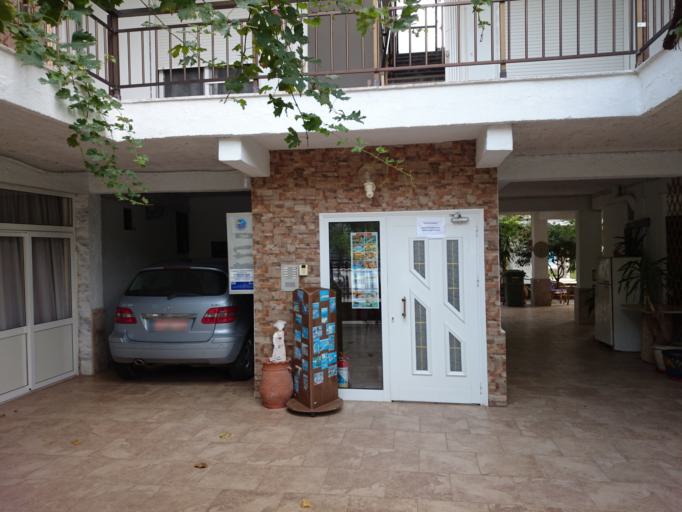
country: GR
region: Central Macedonia
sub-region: Nomos Chalkidikis
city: Nea Moudhania
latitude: 40.2502
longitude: 23.2535
